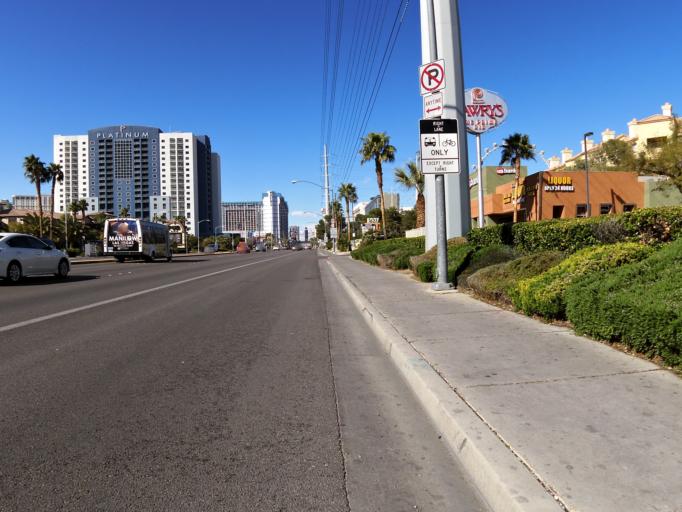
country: US
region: Nevada
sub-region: Clark County
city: Paradise
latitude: 36.1146
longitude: -115.1599
